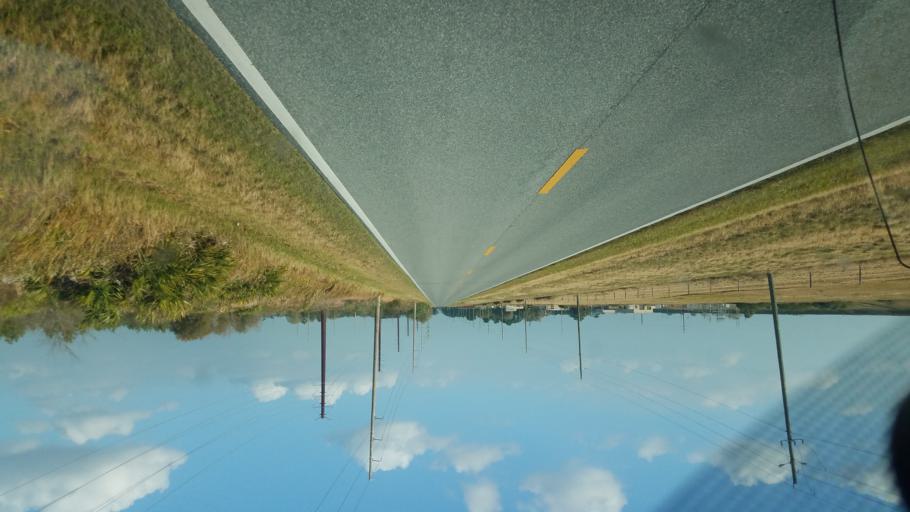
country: US
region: Florida
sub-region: Hardee County
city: Bowling Green
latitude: 27.6250
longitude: -81.9453
